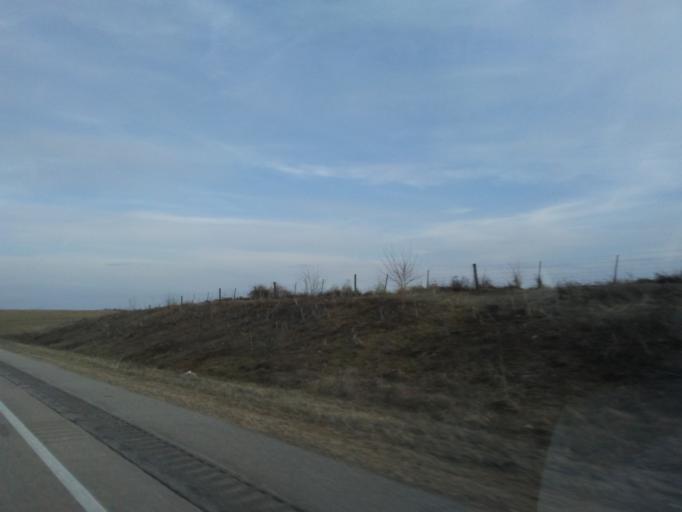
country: US
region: Wisconsin
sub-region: Iowa County
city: Barneveld
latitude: 43.0092
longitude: -89.8611
